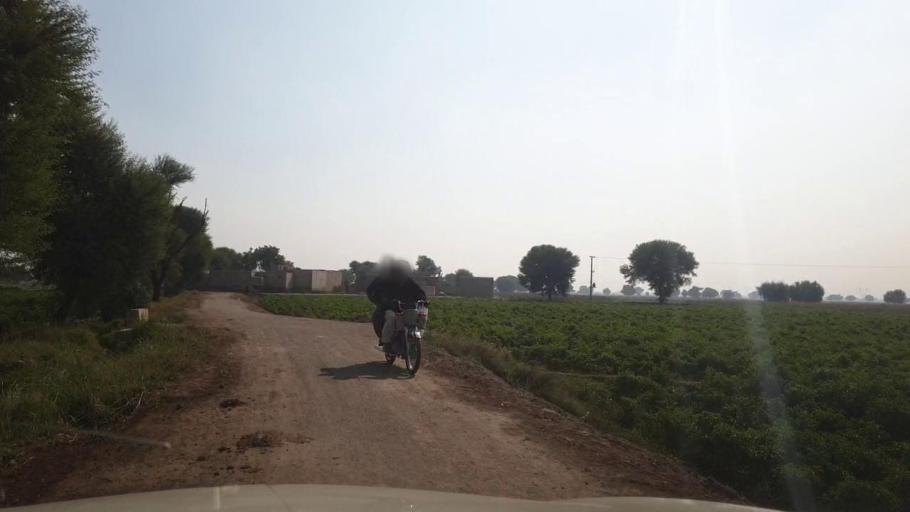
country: PK
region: Sindh
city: Bhan
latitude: 26.5416
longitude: 67.7552
